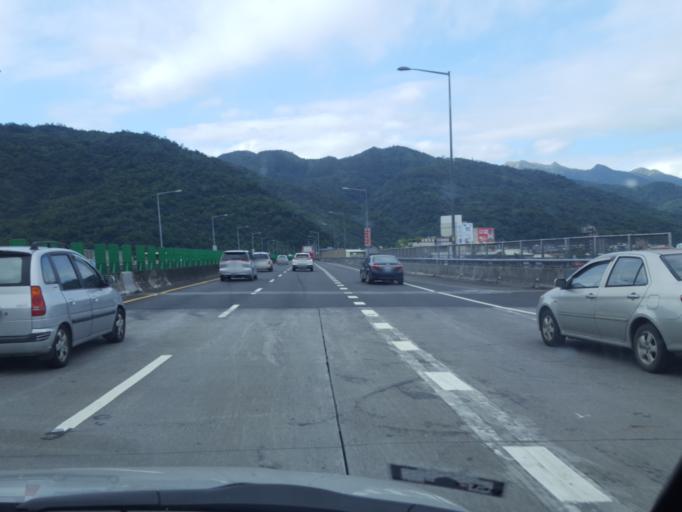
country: TW
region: Taiwan
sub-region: Yilan
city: Yilan
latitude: 24.8358
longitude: 121.7904
